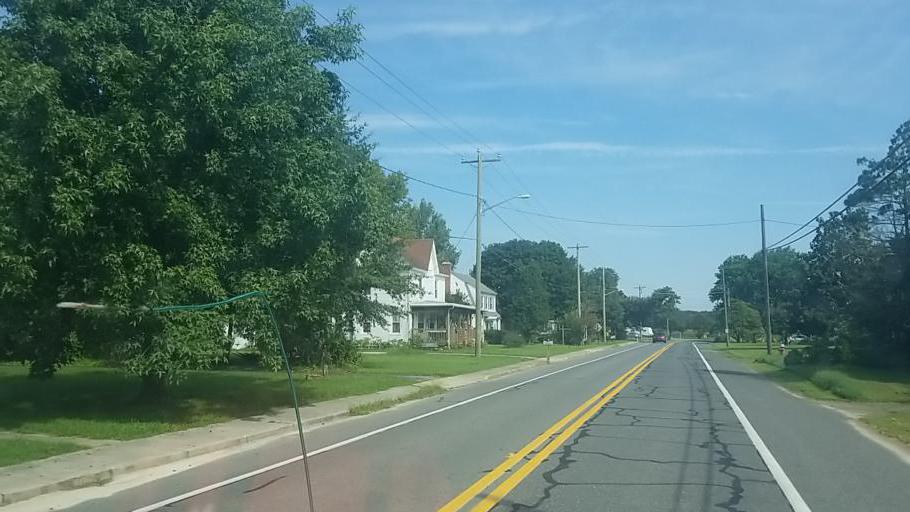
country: US
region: Delaware
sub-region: Sussex County
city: Selbyville
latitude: 38.5237
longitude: -75.2378
